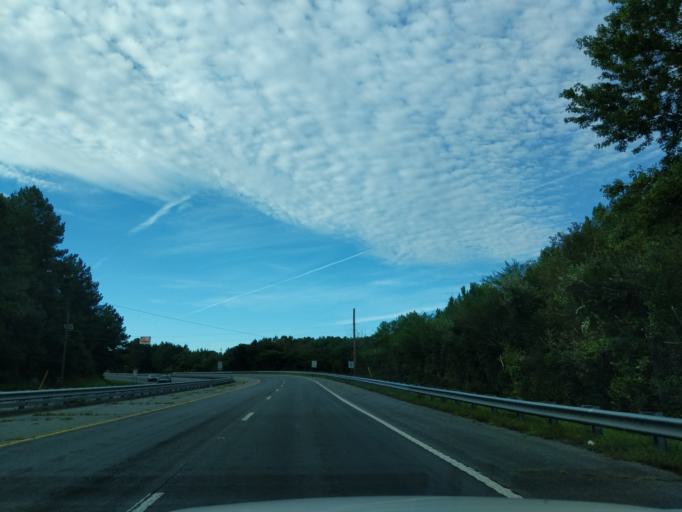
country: US
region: Georgia
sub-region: Fannin County
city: McCaysville
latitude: 35.0221
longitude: -84.3835
